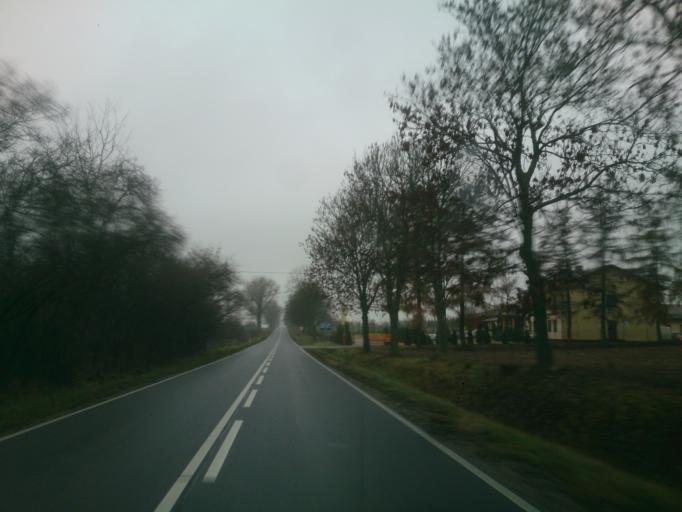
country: PL
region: Kujawsko-Pomorskie
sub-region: Powiat rypinski
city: Rypin
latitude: 53.0902
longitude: 19.4100
